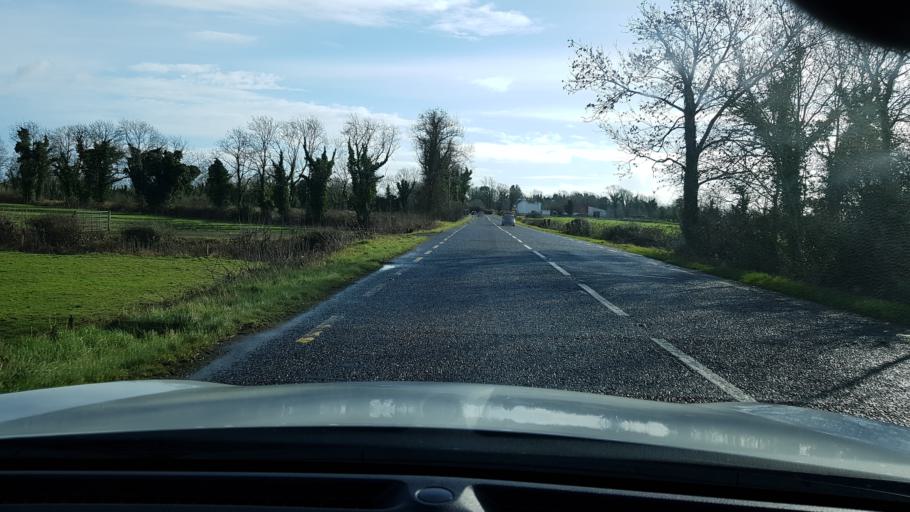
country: IE
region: Leinster
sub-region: An Longfort
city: Longford
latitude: 53.8102
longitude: -7.8899
